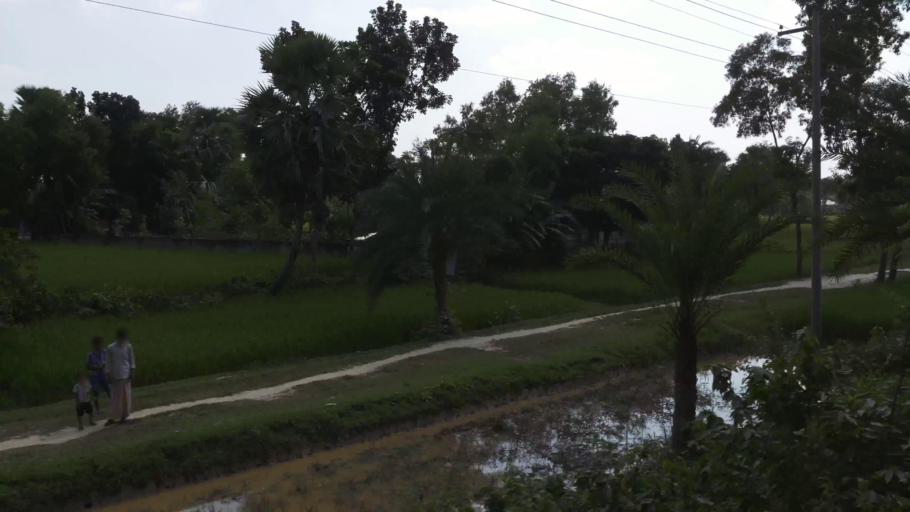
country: BD
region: Dhaka
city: Gafargaon
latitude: 24.2144
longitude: 90.4842
